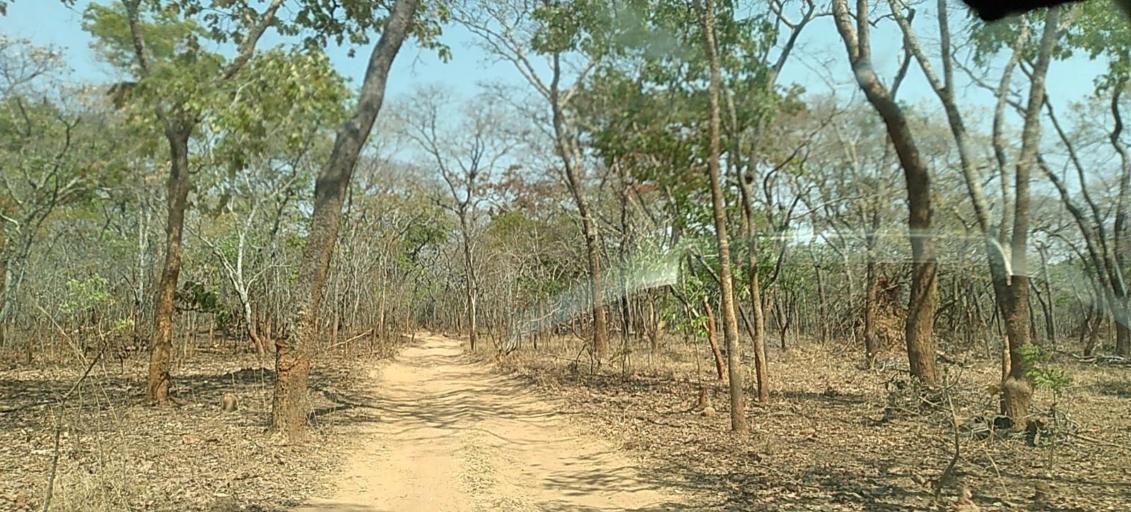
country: ZM
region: North-Western
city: Kasempa
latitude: -13.3928
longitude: 25.6109
